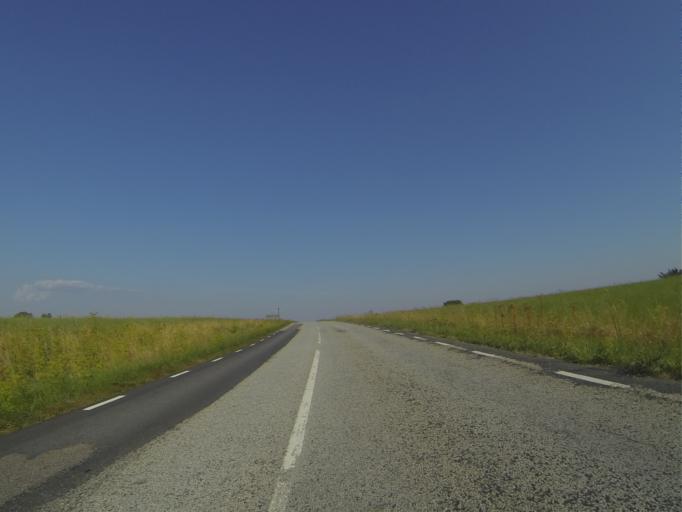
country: SE
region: Skane
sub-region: Svedala Kommun
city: Klagerup
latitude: 55.5846
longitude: 13.2937
